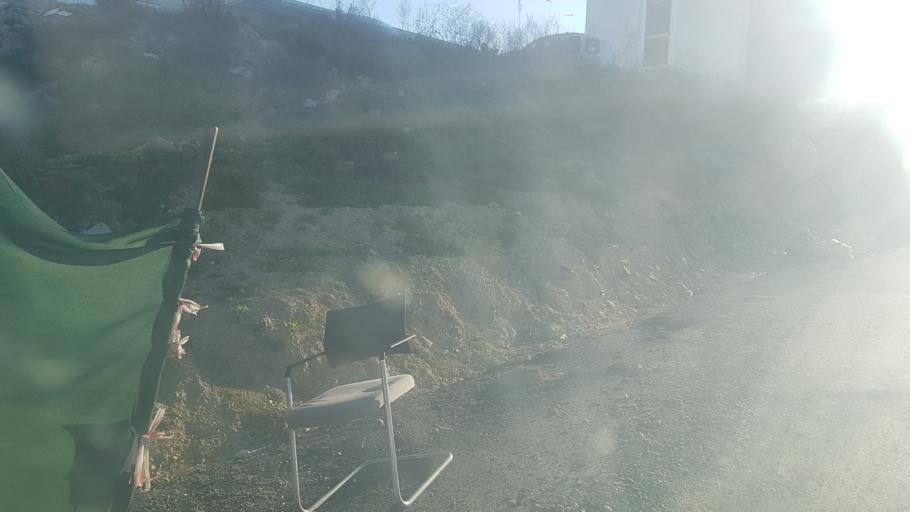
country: TR
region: Adana
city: Seyhan
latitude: 37.0540
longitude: 35.2535
